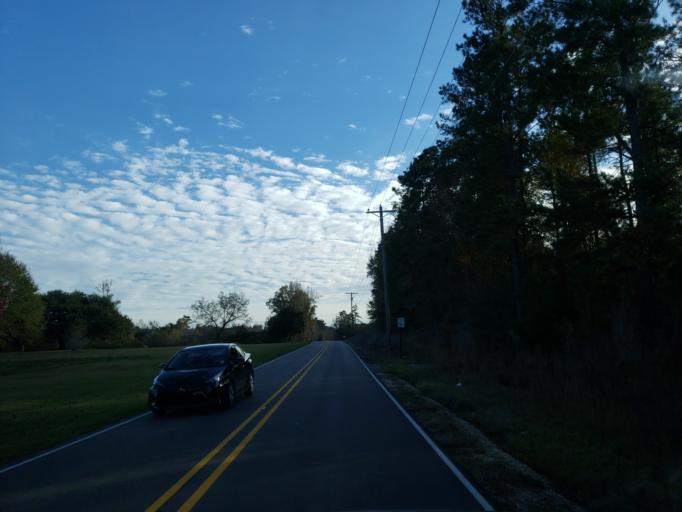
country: US
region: Mississippi
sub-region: Lamar County
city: West Hattiesburg
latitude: 31.3043
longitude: -89.3989
